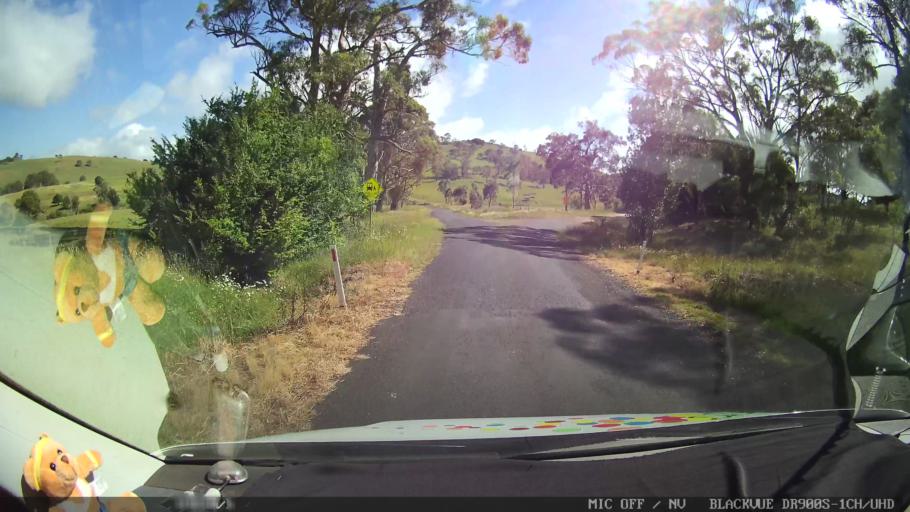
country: AU
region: New South Wales
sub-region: Guyra
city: Guyra
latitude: -30.0120
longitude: 151.6583
